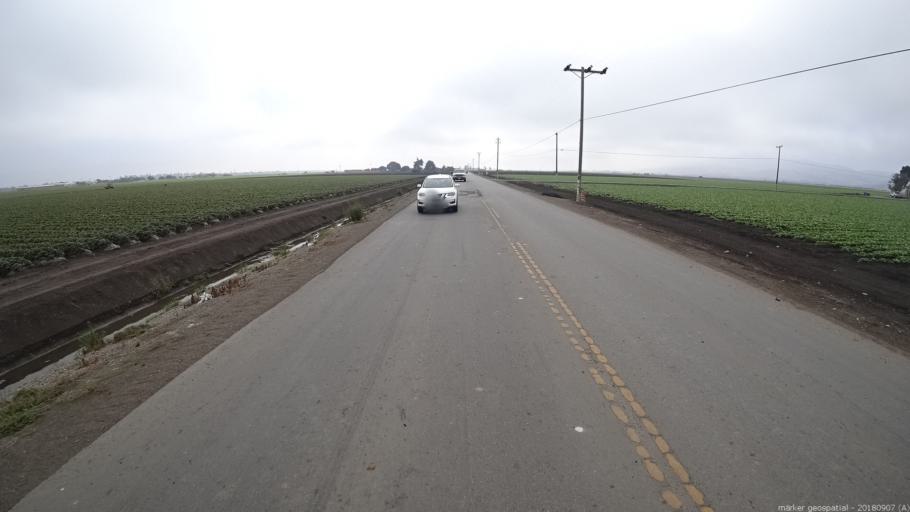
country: US
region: California
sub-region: Monterey County
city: Salinas
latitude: 36.6584
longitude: -121.6912
